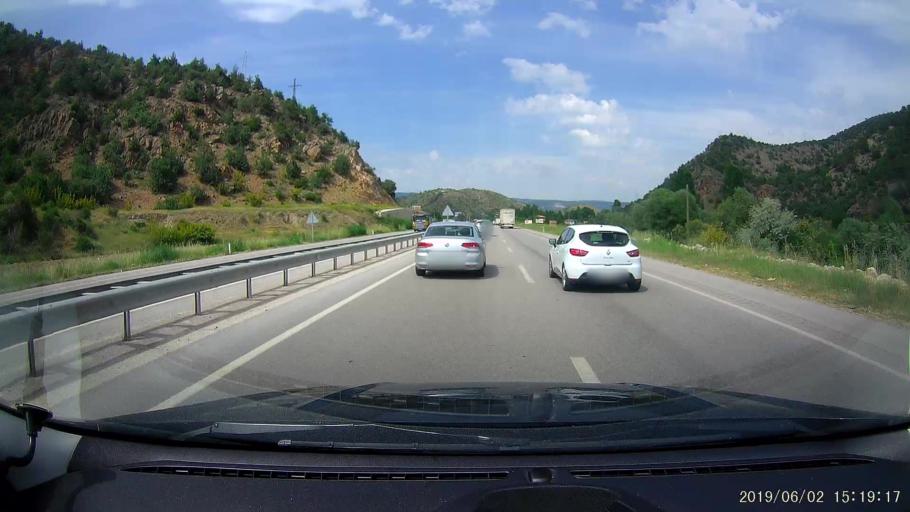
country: TR
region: Corum
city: Osmancik
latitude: 40.9690
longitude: 34.9074
